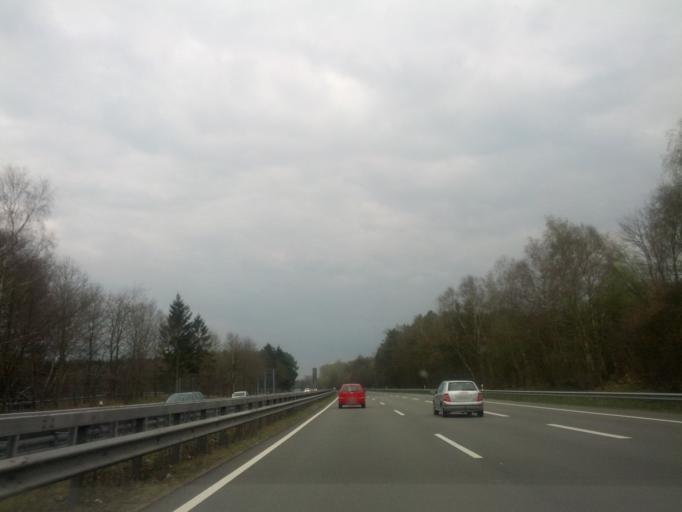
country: DE
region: Lower Saxony
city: Bad Zwischenahn
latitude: 53.2131
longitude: 8.0577
